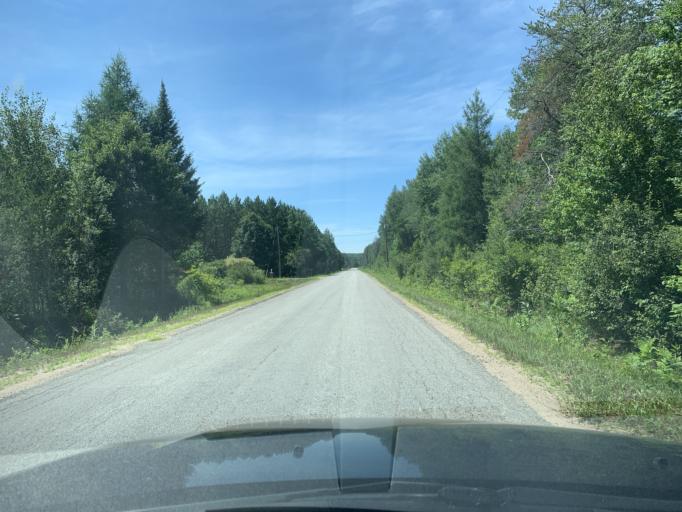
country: CA
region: Ontario
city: Petawawa
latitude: 45.6602
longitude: -77.5943
